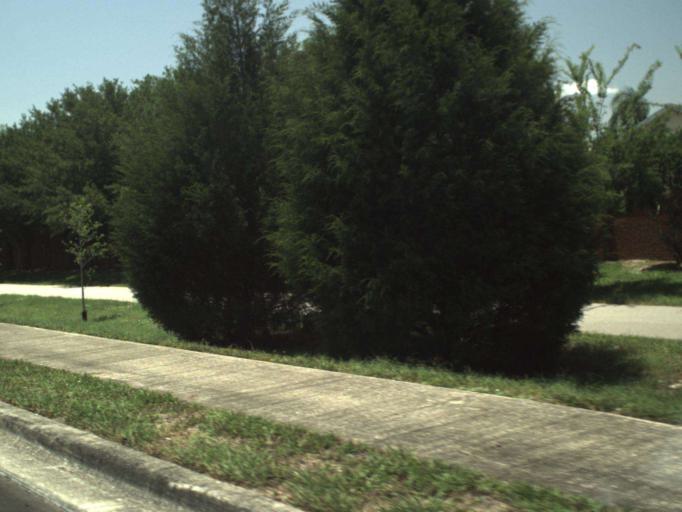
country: US
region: Florida
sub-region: Seminole County
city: Winter Springs
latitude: 28.7047
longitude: -81.2839
